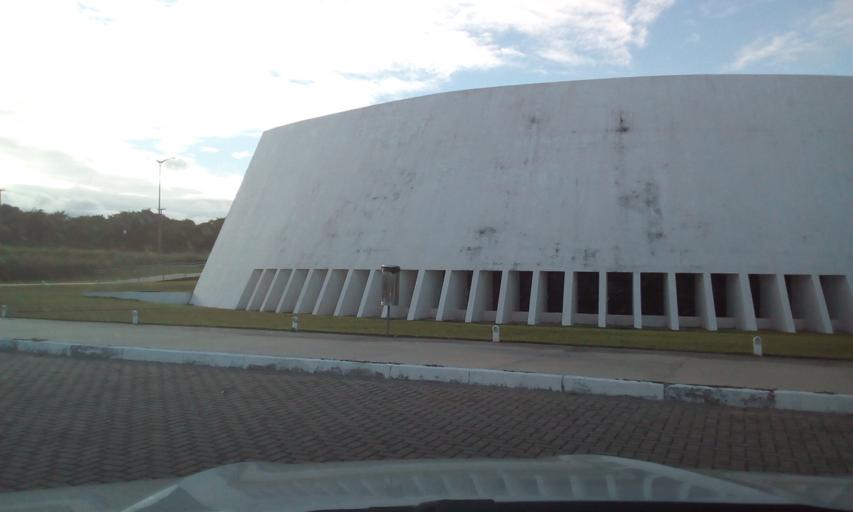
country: BR
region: Paraiba
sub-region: Joao Pessoa
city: Joao Pessoa
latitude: -7.1491
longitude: -34.7980
